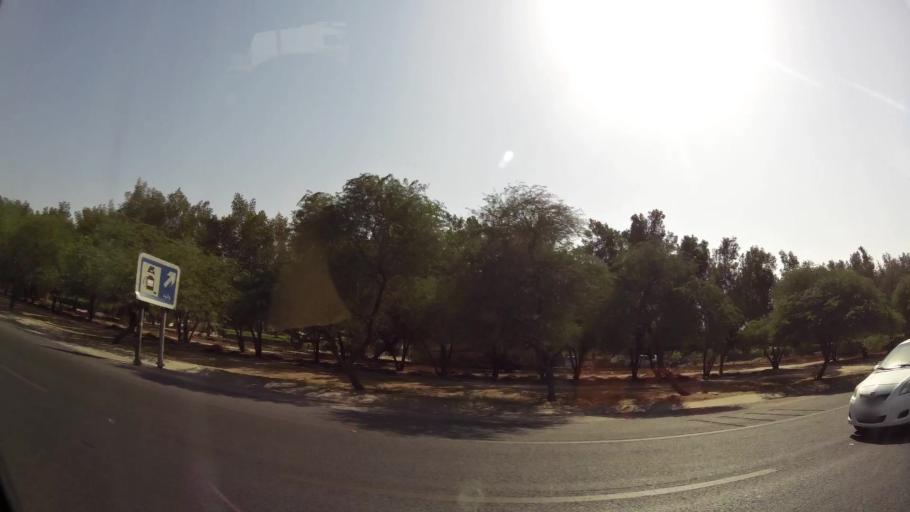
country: KW
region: Mubarak al Kabir
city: Sabah as Salim
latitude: 29.2644
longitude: 48.0607
